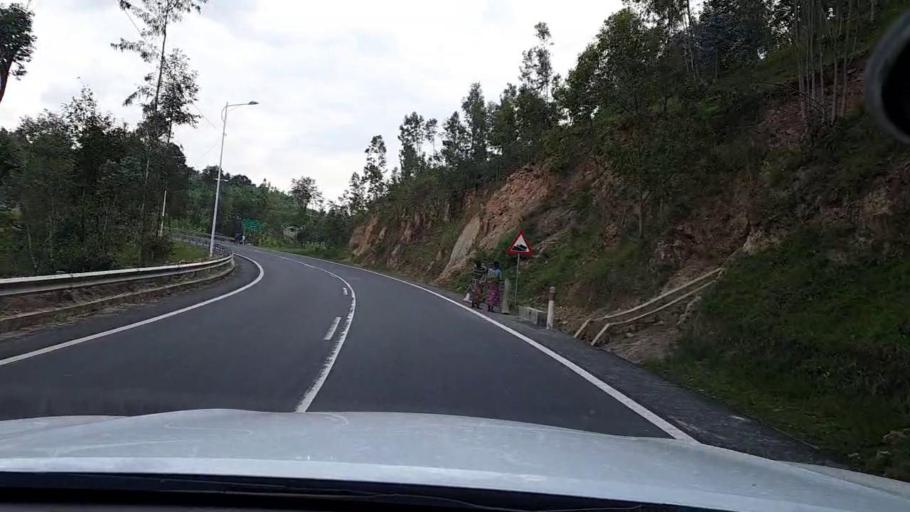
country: RW
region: Western Province
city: Kibuye
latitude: -2.0839
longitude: 29.4155
